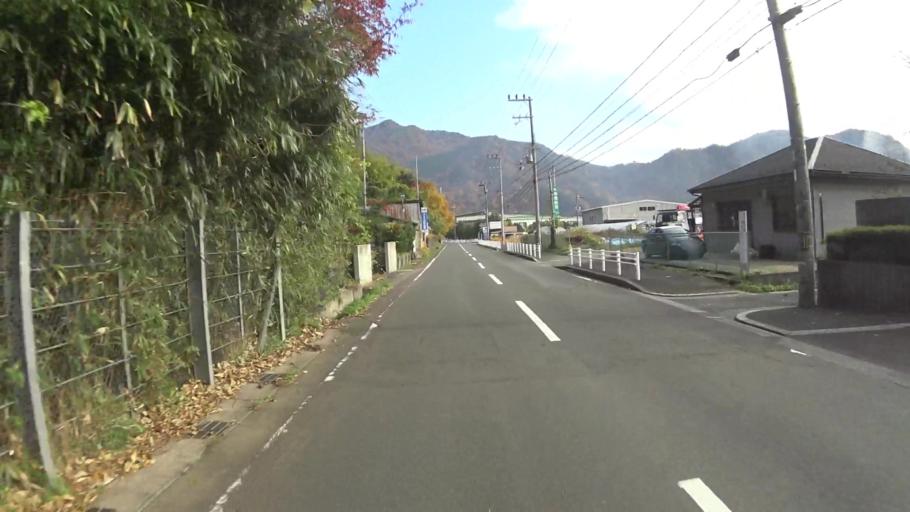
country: JP
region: Kyoto
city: Maizuru
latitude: 35.5181
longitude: 135.3960
